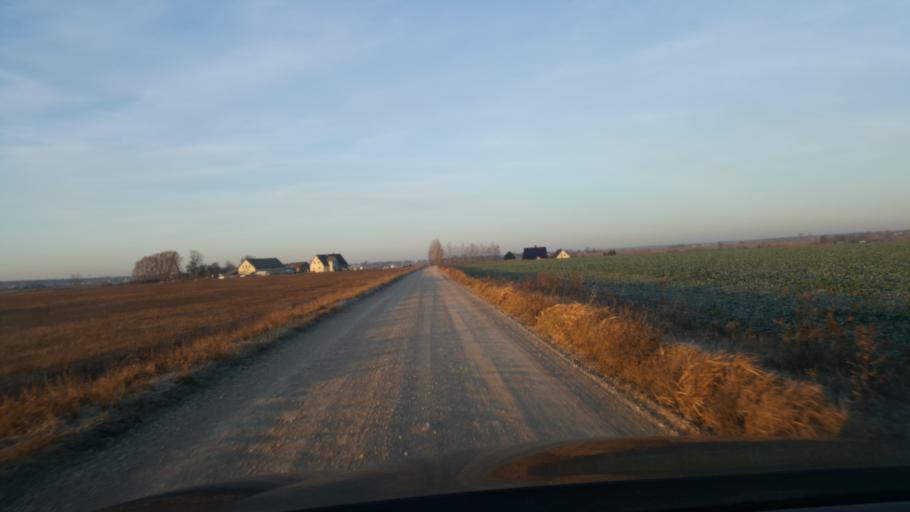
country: LT
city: Prienai
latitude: 54.4839
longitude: 23.9155
